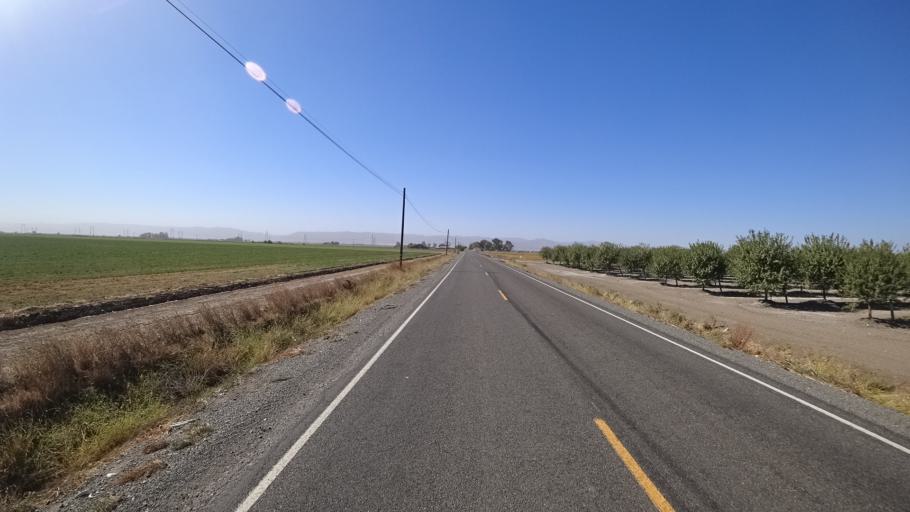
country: US
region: California
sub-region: Yolo County
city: Winters
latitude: 38.5837
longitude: -121.9147
